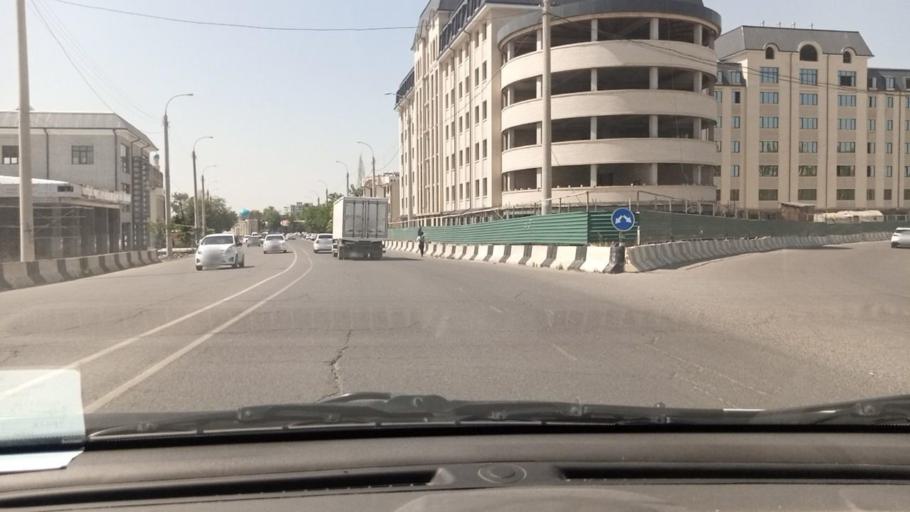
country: UZ
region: Toshkent Shahri
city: Tashkent
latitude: 41.2576
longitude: 69.1914
